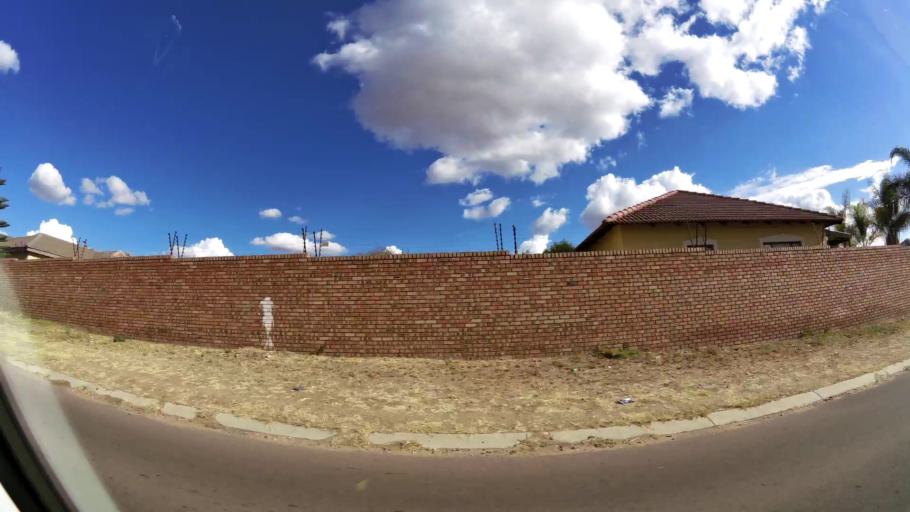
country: ZA
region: Limpopo
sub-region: Capricorn District Municipality
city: Polokwane
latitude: -23.8790
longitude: 29.4869
